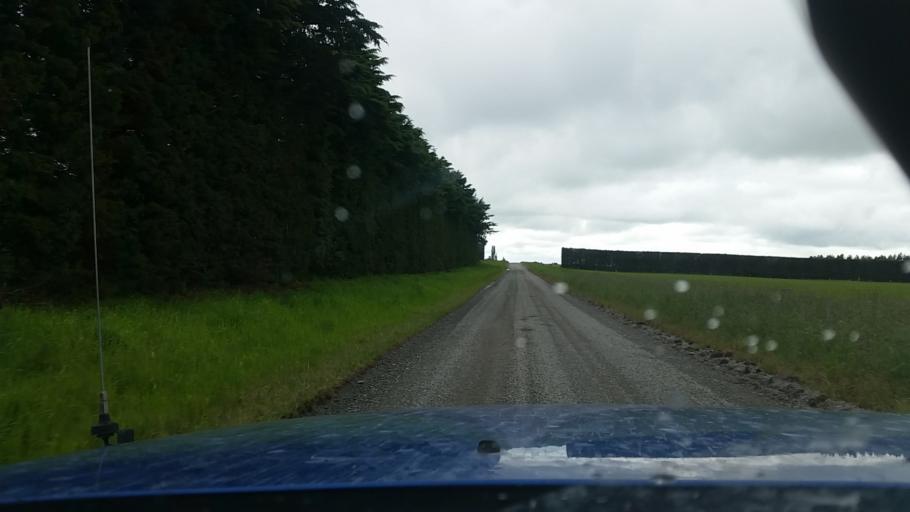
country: NZ
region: Canterbury
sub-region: Ashburton District
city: Methven
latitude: -43.6920
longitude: 171.3977
